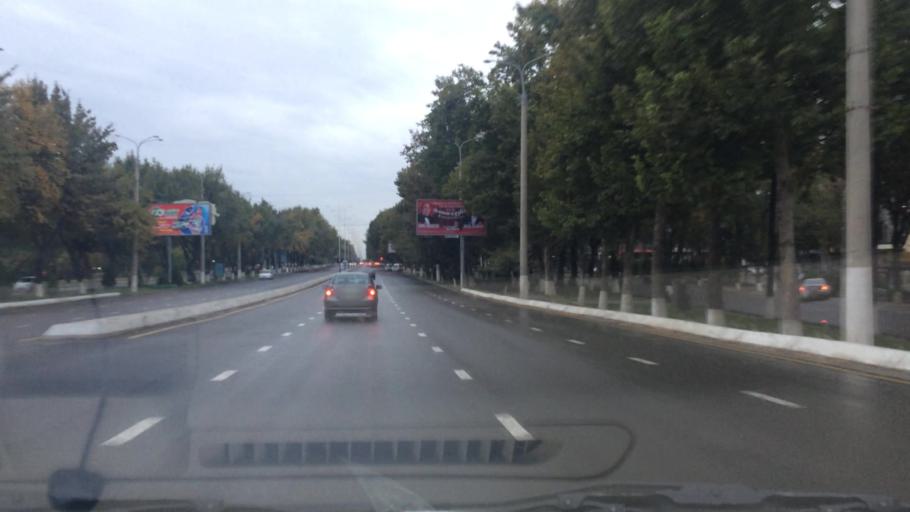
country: UZ
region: Toshkent Shahri
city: Tashkent
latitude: 41.2726
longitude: 69.2032
